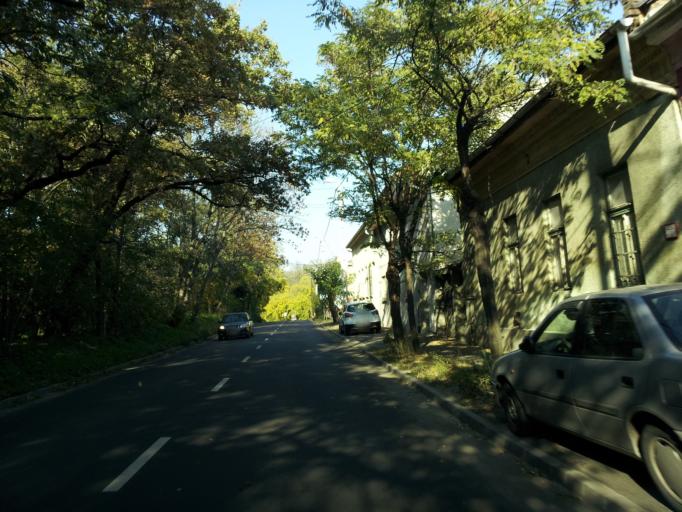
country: HU
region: Budapest
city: Budapest XVIII. keruelet
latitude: 47.4662
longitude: 19.1784
